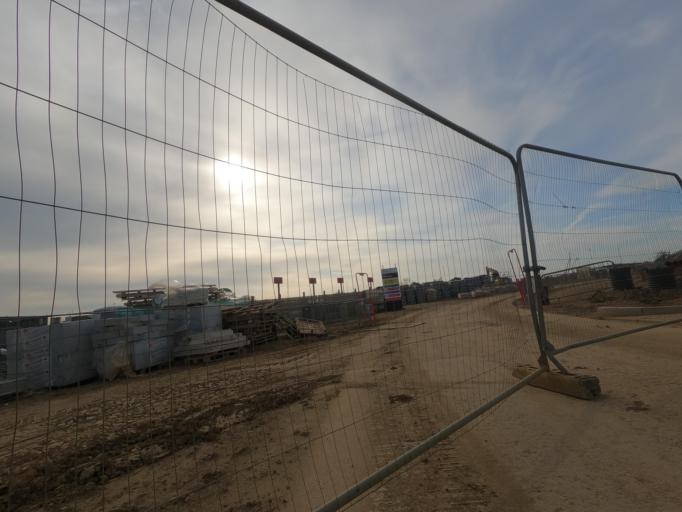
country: GB
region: England
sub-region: Newcastle upon Tyne
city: Hazlerigg
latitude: 55.0288
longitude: -1.6624
